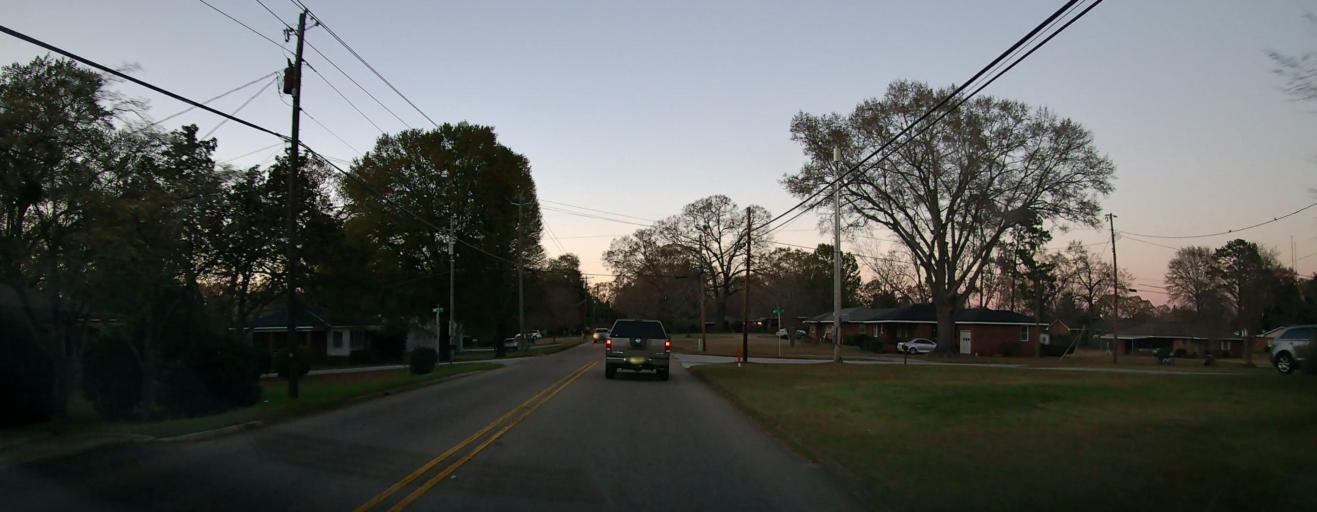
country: US
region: Alabama
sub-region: Russell County
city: Phenix City
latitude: 32.5062
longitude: -85.0195
